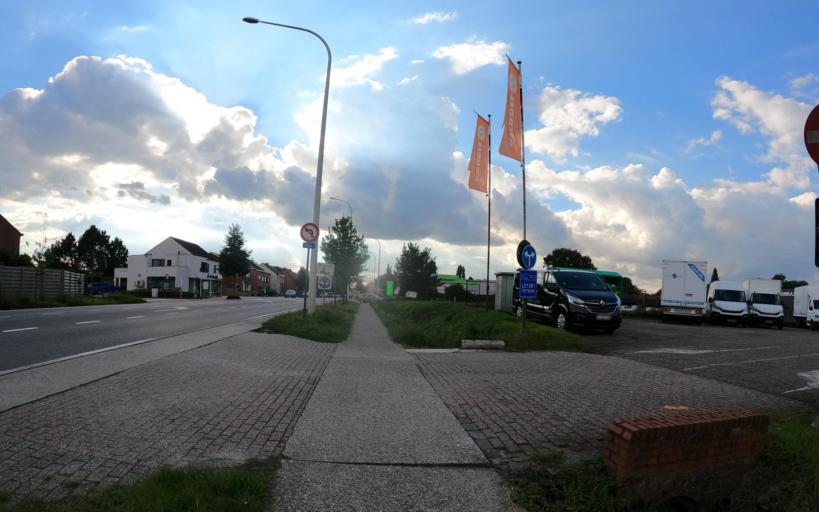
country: BE
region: Flanders
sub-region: Provincie Antwerpen
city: Oostmalle
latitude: 51.2983
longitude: 4.7038
